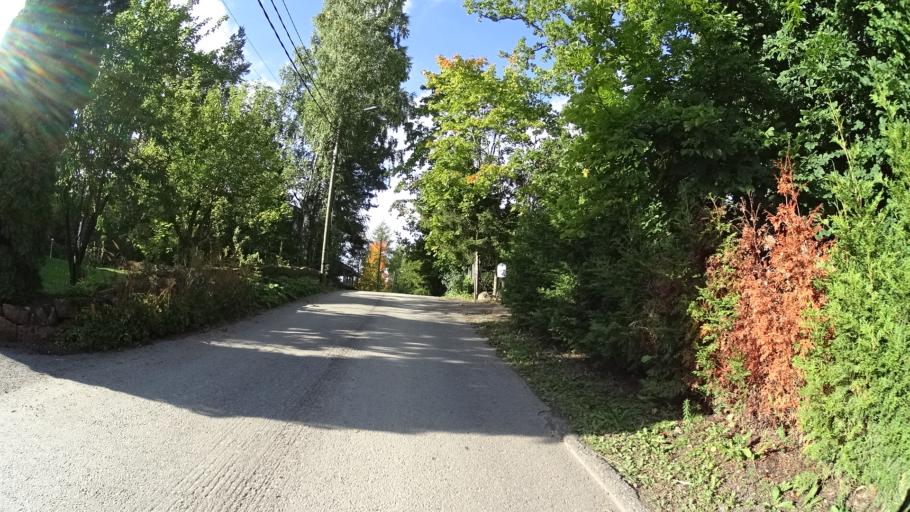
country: FI
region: Uusimaa
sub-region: Helsinki
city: Kilo
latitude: 60.2483
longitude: 24.7639
